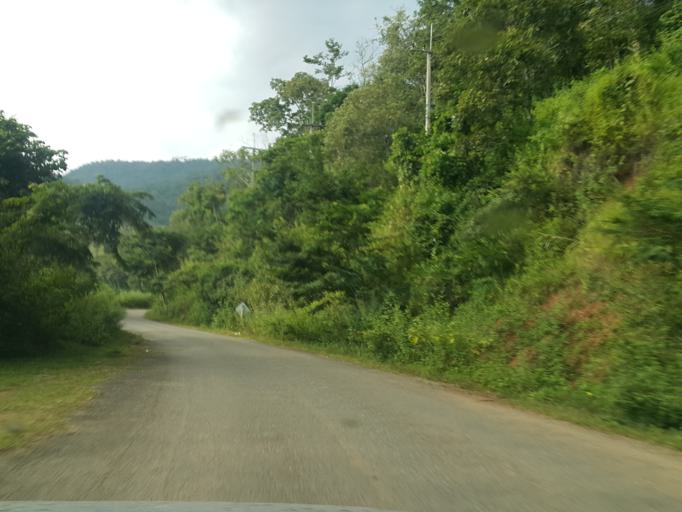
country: TH
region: Mae Hong Son
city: Khun Yuam
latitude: 18.7535
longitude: 98.1920
